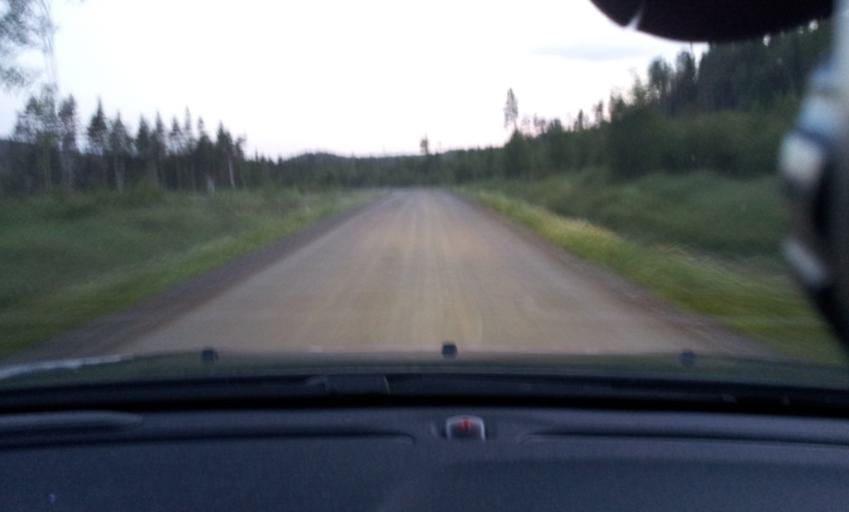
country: SE
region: Vaesternorrland
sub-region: Ange Kommun
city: Fransta
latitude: 62.7764
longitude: 15.9517
